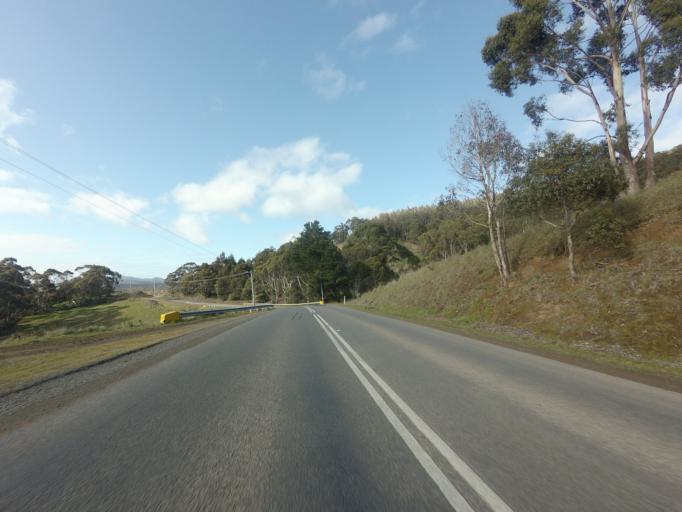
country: AU
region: Tasmania
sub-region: Huon Valley
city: Geeveston
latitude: -43.1809
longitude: 146.9517
